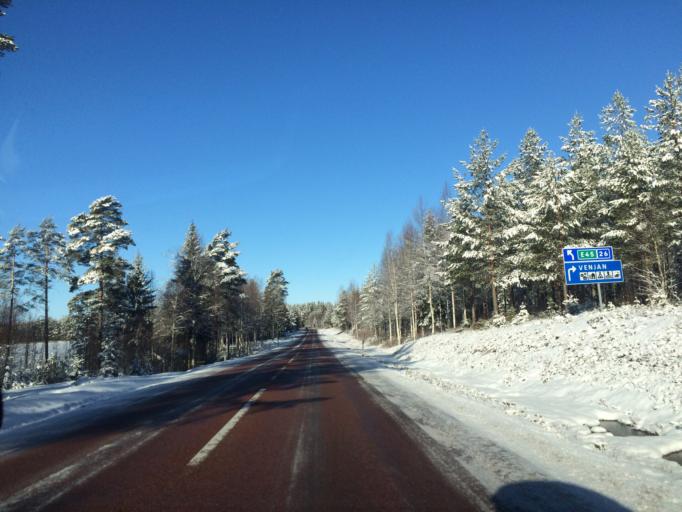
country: SE
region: Dalarna
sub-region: Vansbro Kommun
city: Vansbro
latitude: 60.8459
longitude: 14.1675
